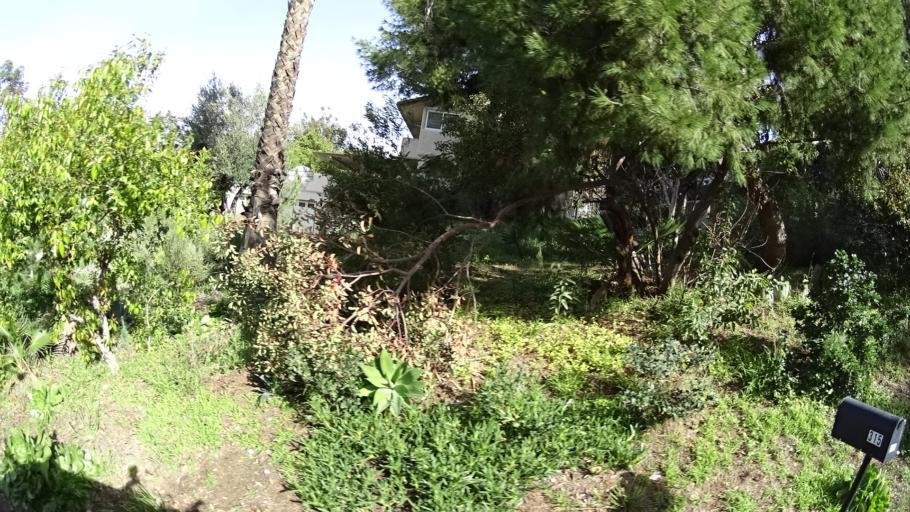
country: US
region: California
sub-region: Orange County
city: Yorba Linda
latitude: 33.8580
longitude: -117.7599
